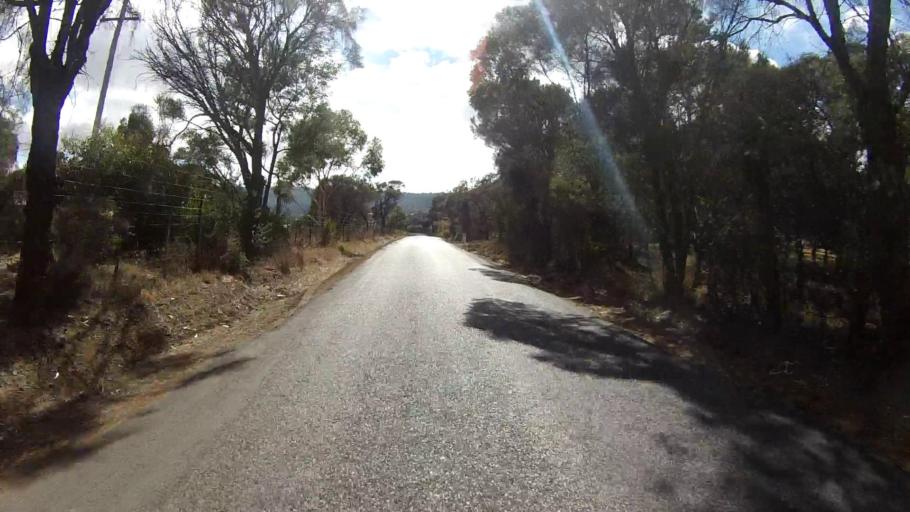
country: AU
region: Tasmania
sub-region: Brighton
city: Old Beach
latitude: -42.7719
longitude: 147.2896
